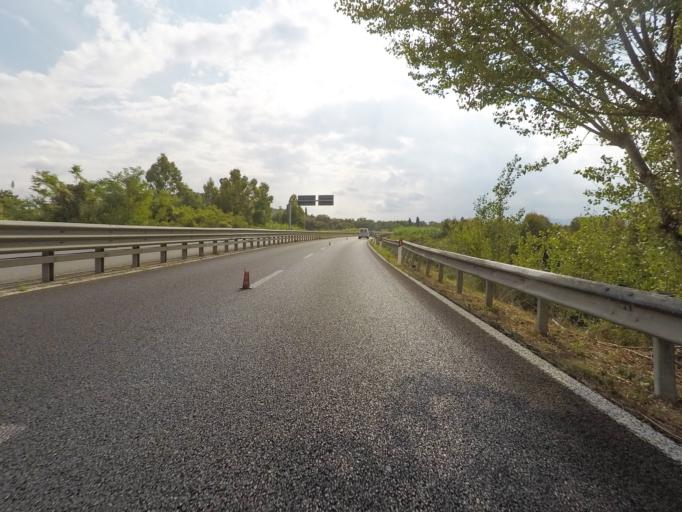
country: IT
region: Tuscany
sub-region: Provincia di Grosseto
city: Grosseto
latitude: 42.7135
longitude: 11.1444
